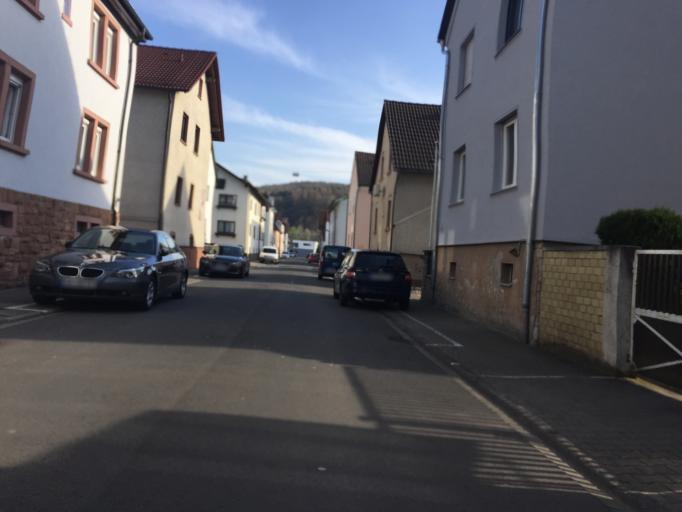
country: DE
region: Bavaria
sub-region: Regierungsbezirk Unterfranken
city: Hosbach
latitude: 50.0017
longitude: 9.1986
